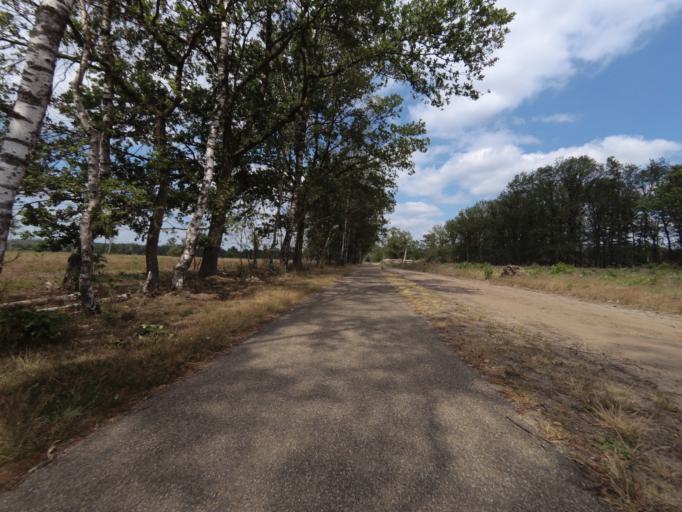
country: NL
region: Overijssel
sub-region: Gemeente Hof van Twente
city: Markelo
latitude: 52.3414
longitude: 6.4528
